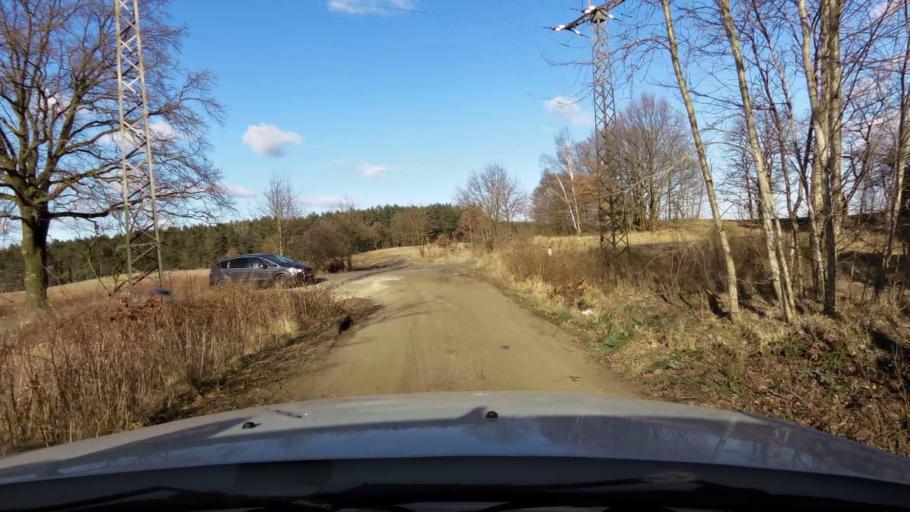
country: PL
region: West Pomeranian Voivodeship
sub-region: Powiat choszczenski
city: Choszczno
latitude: 53.1619
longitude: 15.3784
